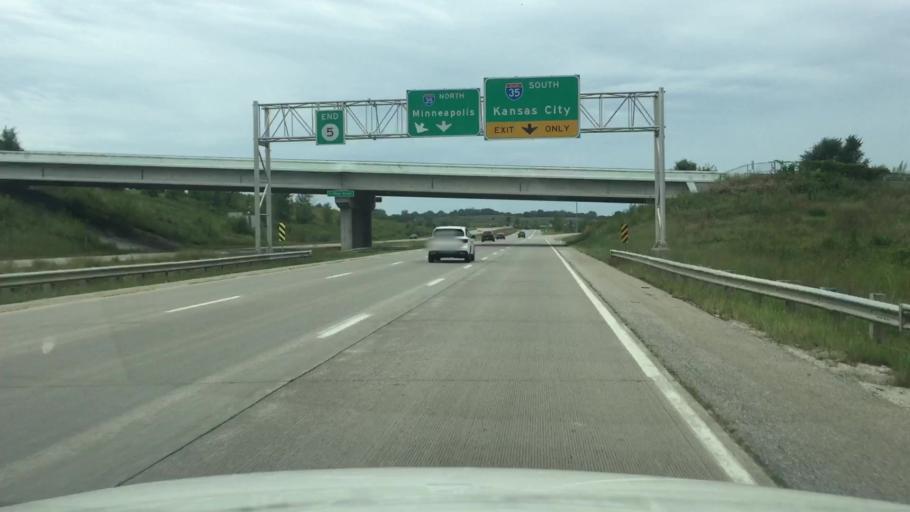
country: US
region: Iowa
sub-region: Polk County
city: West Des Moines
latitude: 41.5230
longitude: -93.7598
